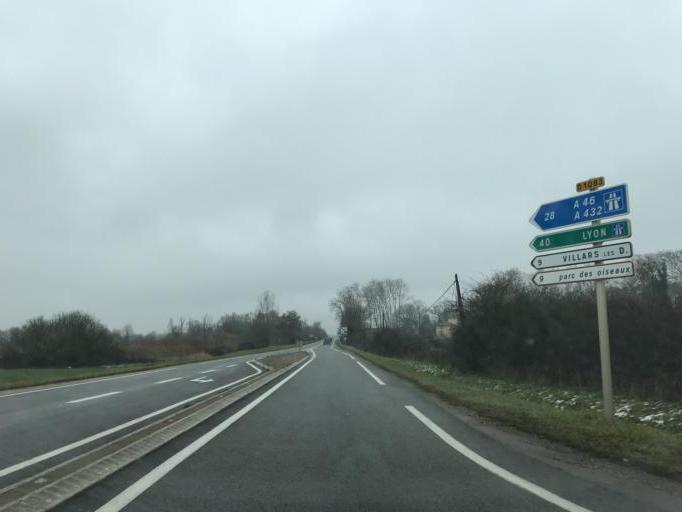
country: FR
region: Rhone-Alpes
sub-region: Departement de l'Ain
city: Saint-Paul-de-Varax
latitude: 46.0643
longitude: 5.0844
